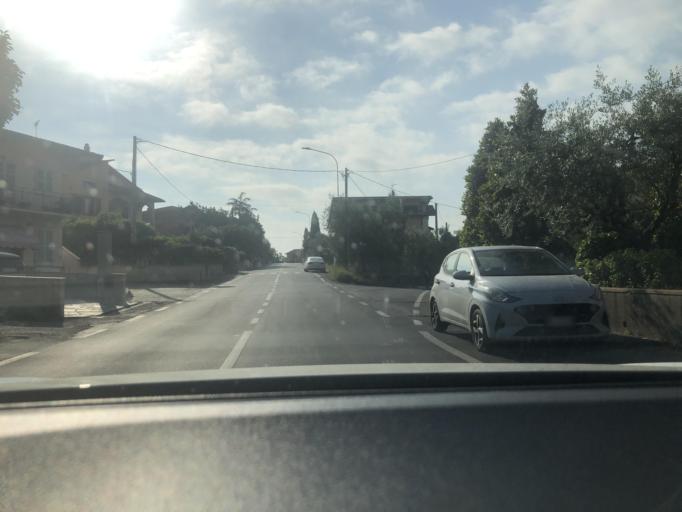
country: IT
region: Tuscany
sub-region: Provincia di Pistoia
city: San Rocco
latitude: 43.8034
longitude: 10.8529
